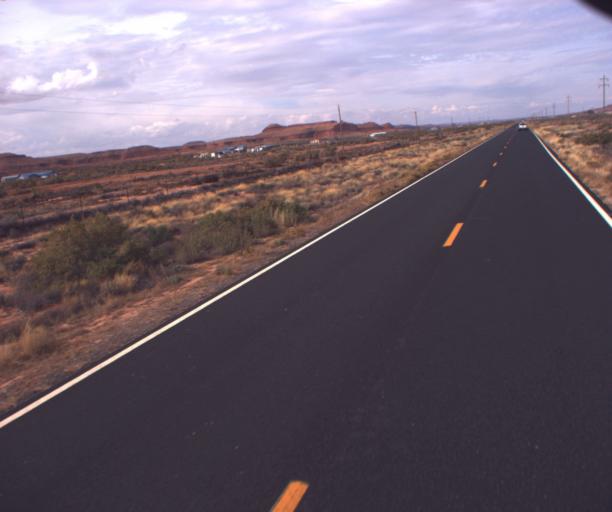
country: US
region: Arizona
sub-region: Apache County
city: Many Farms
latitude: 36.6903
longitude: -109.6095
